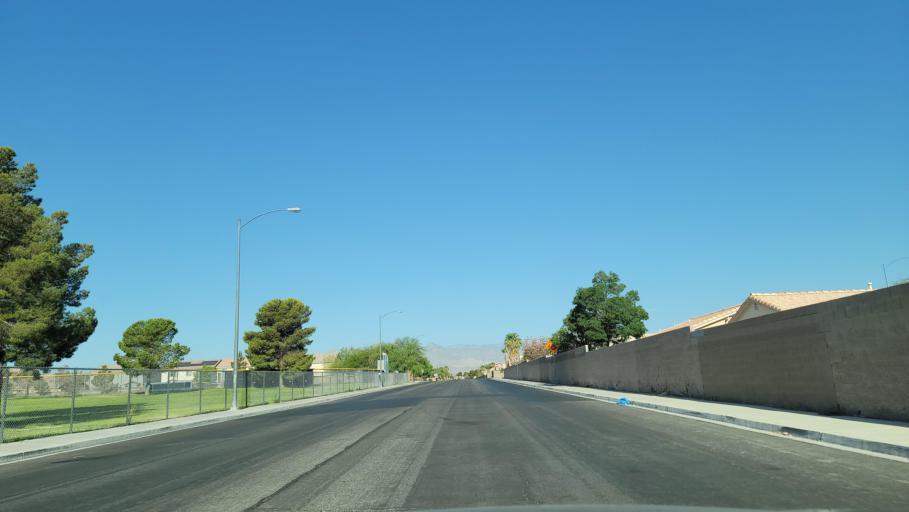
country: US
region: Nevada
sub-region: Clark County
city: North Las Vegas
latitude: 36.2358
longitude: -115.1829
